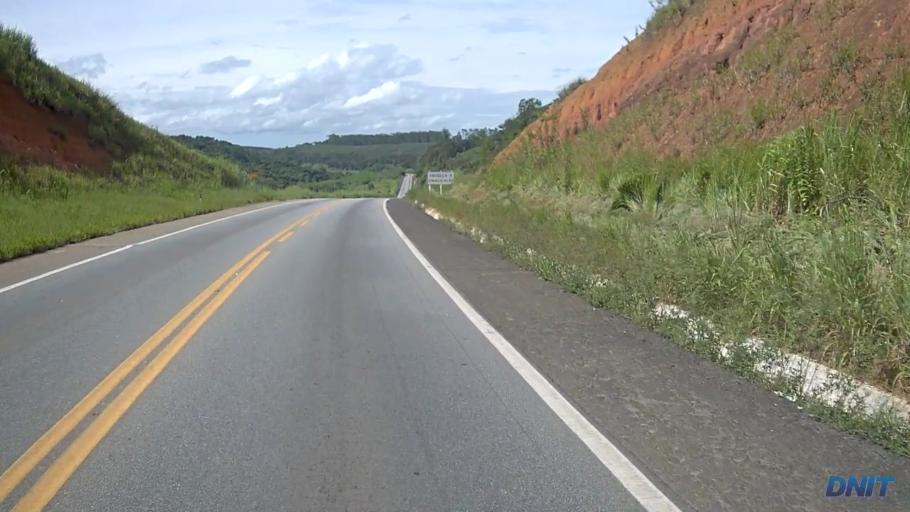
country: BR
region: Minas Gerais
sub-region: Ipatinga
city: Ipatinga
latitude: -19.4145
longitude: -42.4915
